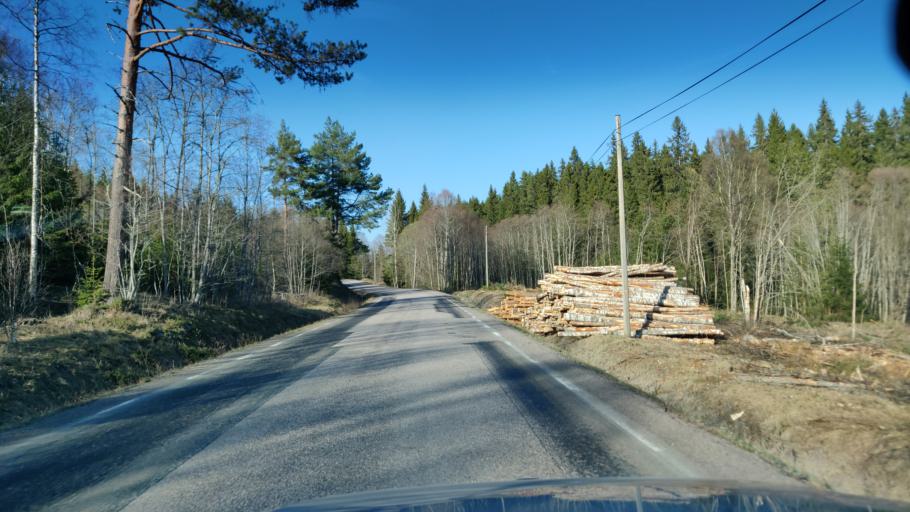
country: SE
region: Vaermland
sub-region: Sunne Kommun
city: Sunne
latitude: 59.9865
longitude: 13.2681
